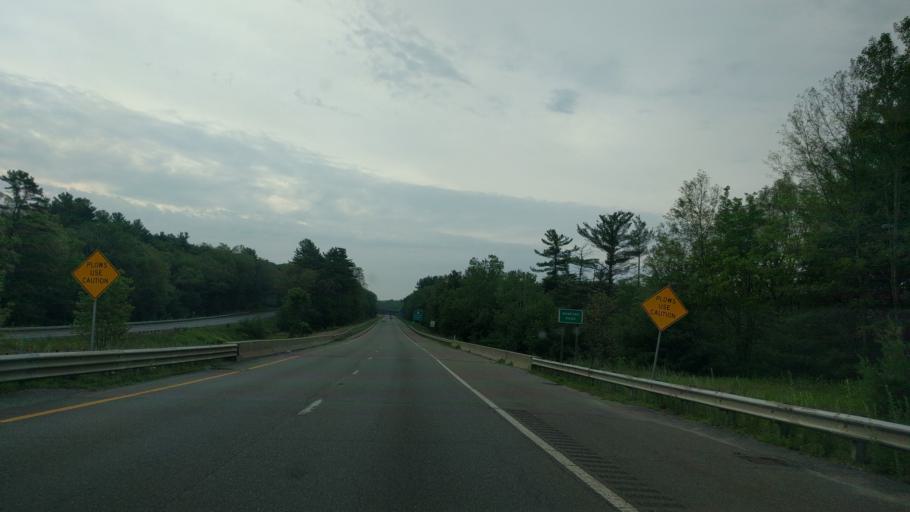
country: US
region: Massachusetts
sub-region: Worcester County
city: East Douglas
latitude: 42.0831
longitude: -71.6905
